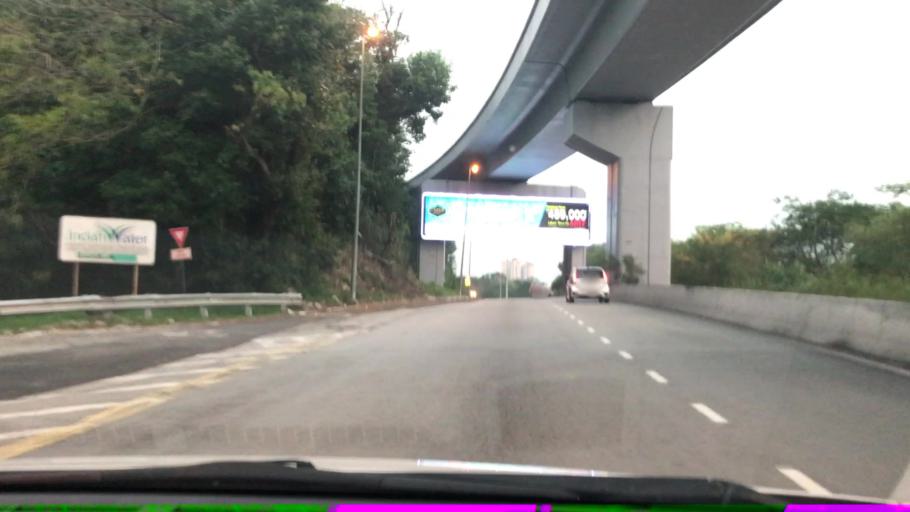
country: MY
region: Selangor
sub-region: Petaling
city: Petaling Jaya
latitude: 3.1339
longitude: 101.6334
